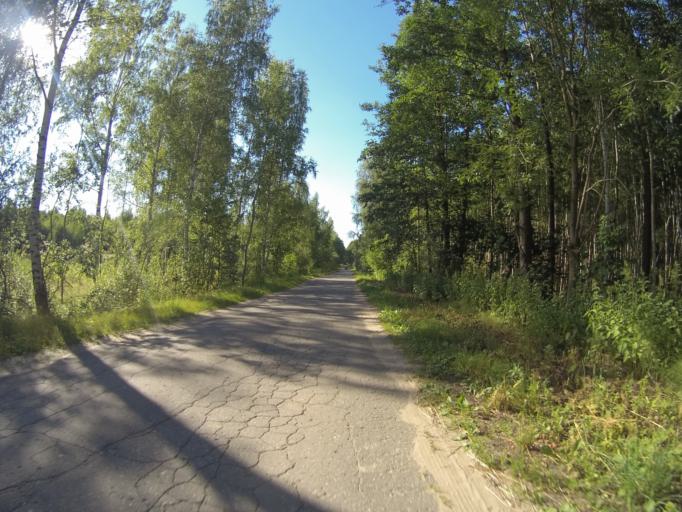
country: RU
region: Vladimir
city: Raduzhnyy
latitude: 56.0070
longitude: 40.3614
